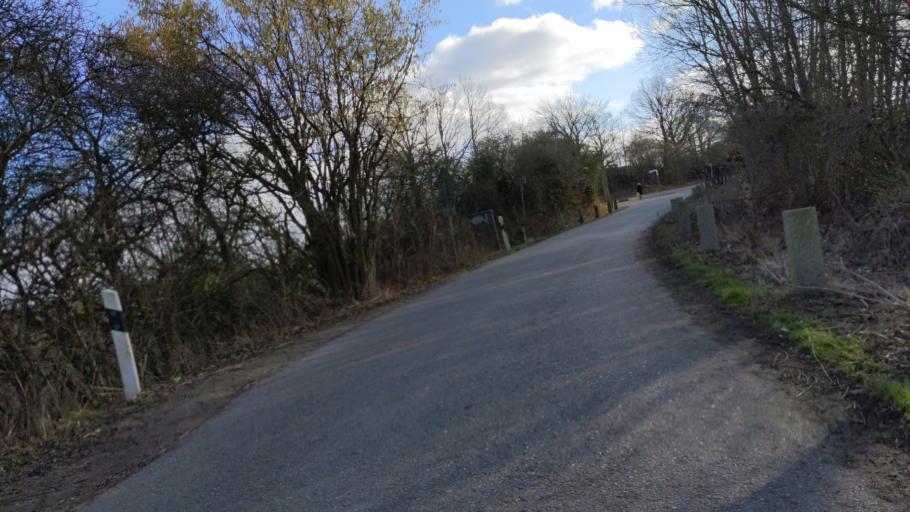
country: DE
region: Schleswig-Holstein
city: Timmendorfer Strand
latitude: 53.9961
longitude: 10.7552
